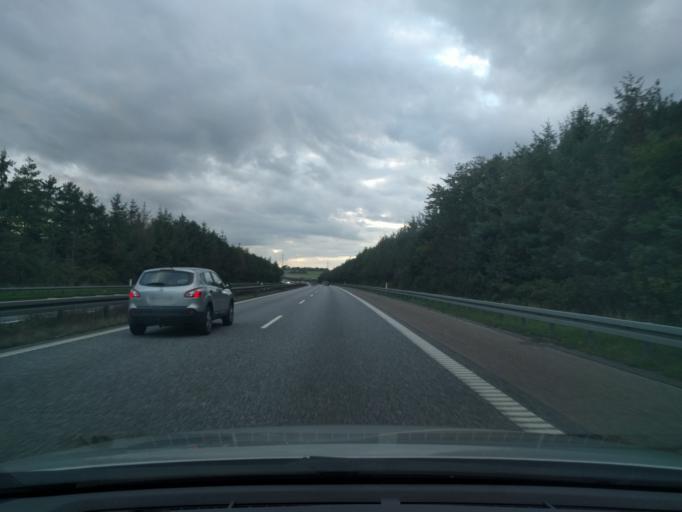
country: DK
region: Zealand
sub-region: Ringsted Kommune
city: Ringsted
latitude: 55.4571
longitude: 11.7704
